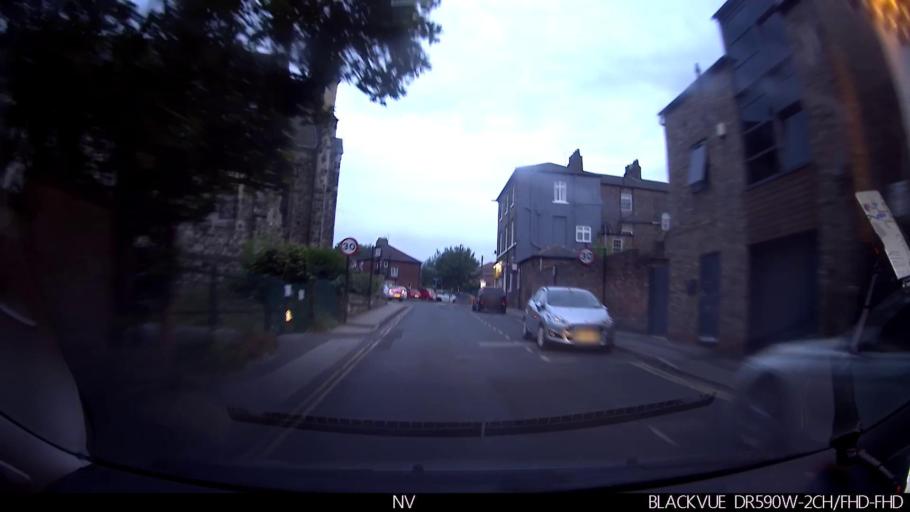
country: GB
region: England
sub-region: City of York
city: York
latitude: 53.9542
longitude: -1.1000
